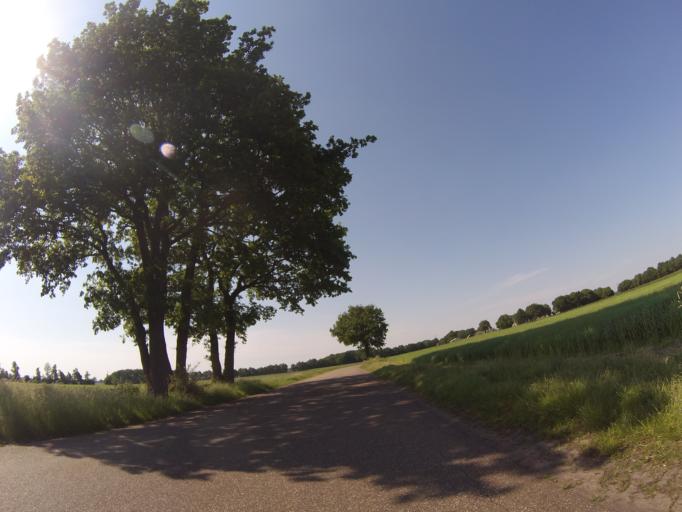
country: NL
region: Drenthe
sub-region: Gemeente Coevorden
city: Dalen
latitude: 52.7104
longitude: 6.8037
